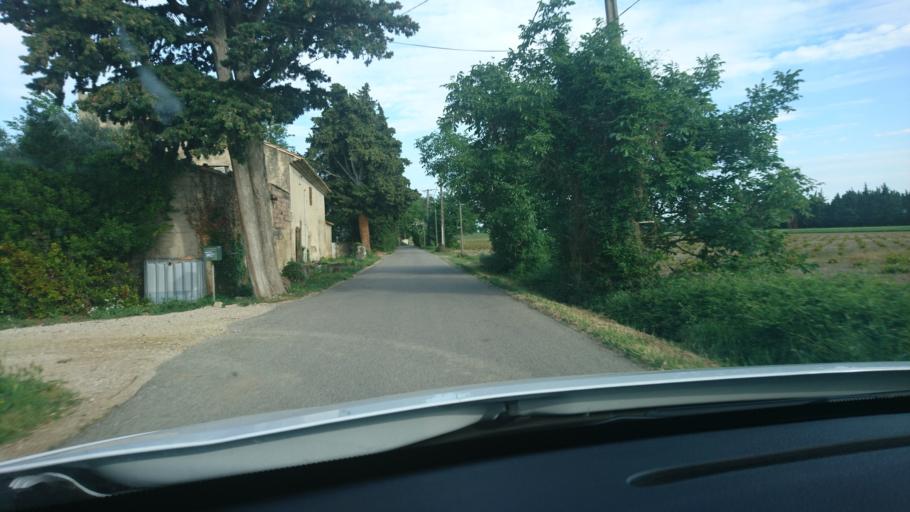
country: FR
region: Provence-Alpes-Cote d'Azur
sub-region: Departement du Vaucluse
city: Jonquieres
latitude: 44.1318
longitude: 4.8845
